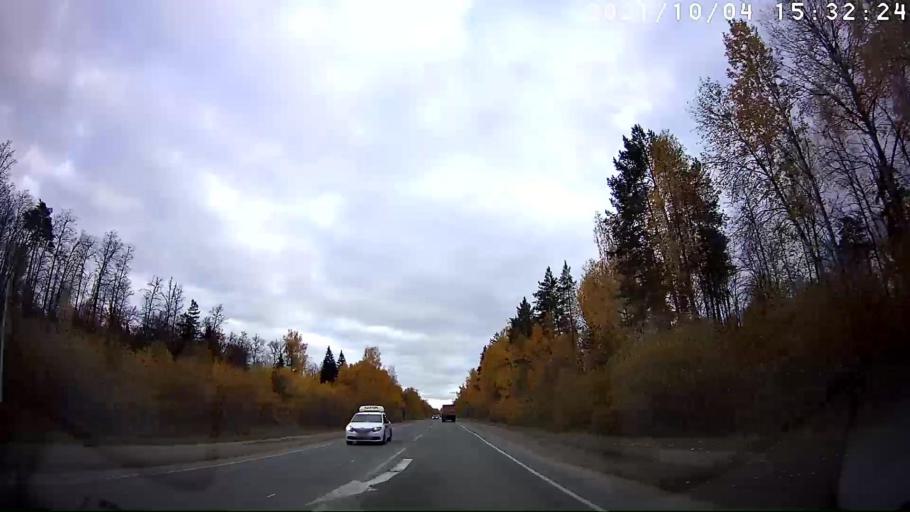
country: RU
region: Mariy-El
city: Yoshkar-Ola
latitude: 56.5695
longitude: 47.9722
